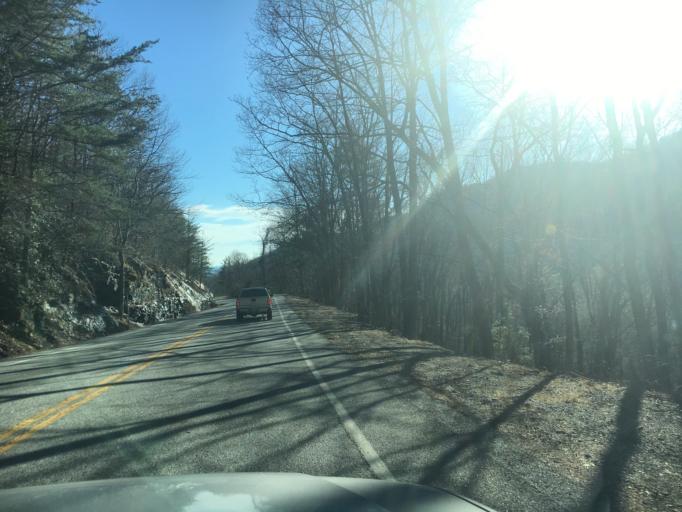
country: US
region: Georgia
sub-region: Union County
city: Blairsville
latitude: 34.7261
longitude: -83.9130
